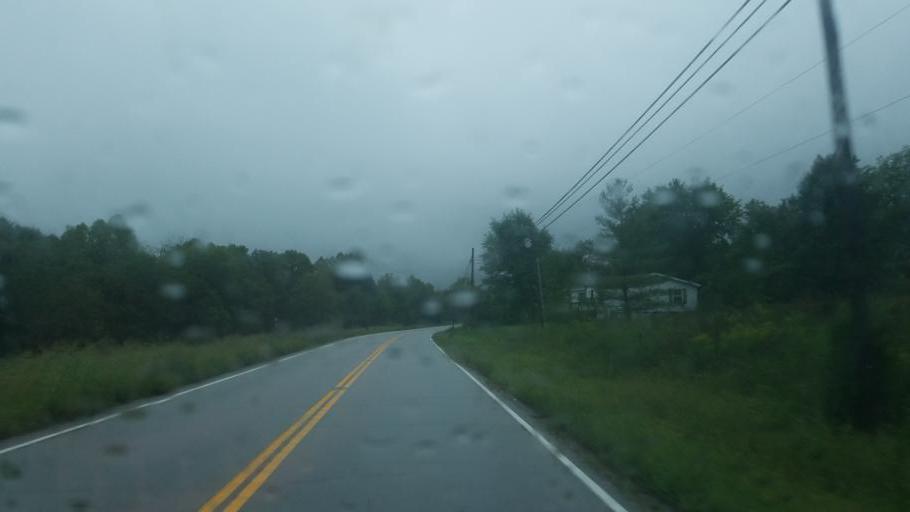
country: US
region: Kentucky
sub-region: Fleming County
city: Flemingsburg
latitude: 38.3705
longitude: -83.6266
